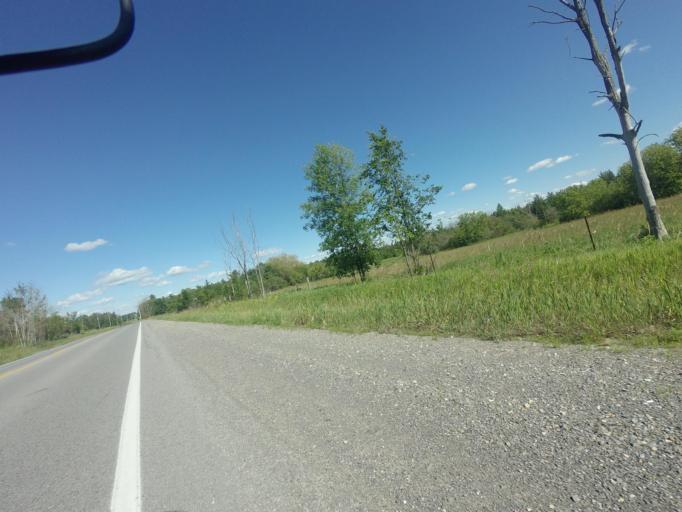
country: CA
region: Ontario
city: Arnprior
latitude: 45.4093
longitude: -76.4525
